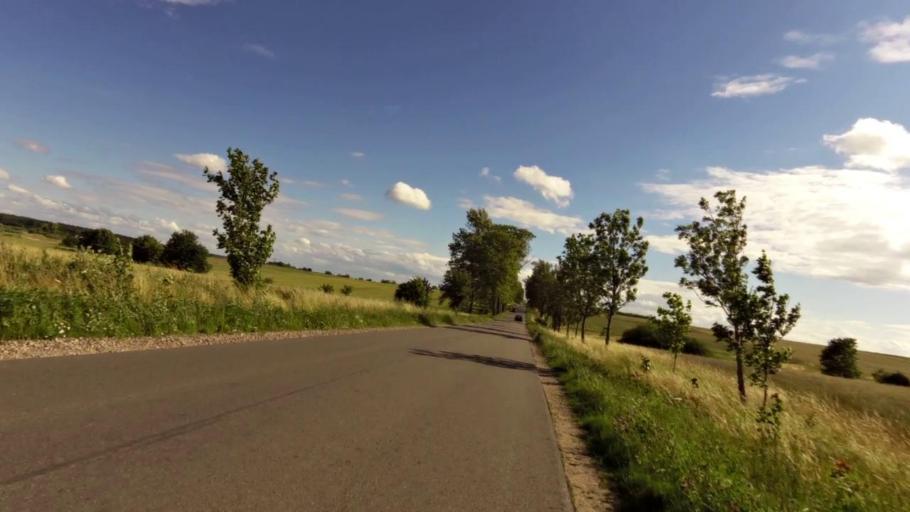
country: PL
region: West Pomeranian Voivodeship
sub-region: Powiat slawienski
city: Slawno
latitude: 54.4463
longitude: 16.7361
